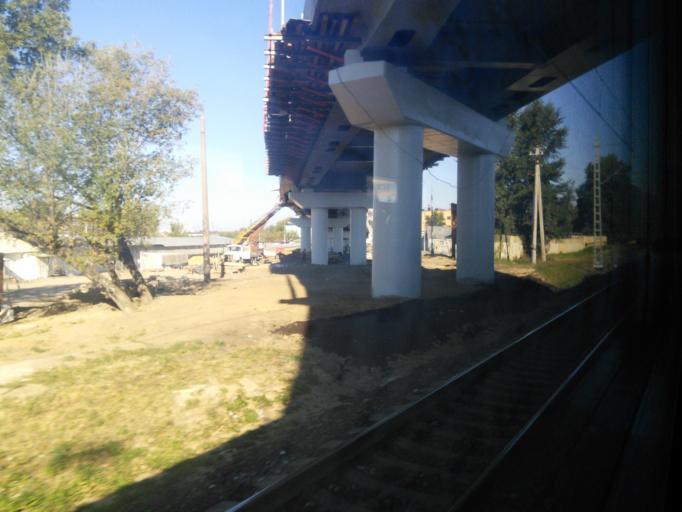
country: RU
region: Moscow
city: Tekstil'shchiki
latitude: 55.7162
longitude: 37.7240
